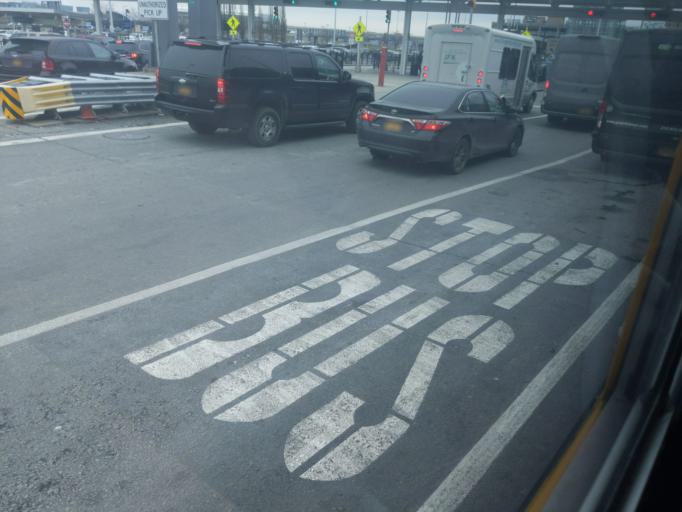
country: US
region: New York
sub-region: Nassau County
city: Inwood
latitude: 40.6431
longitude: -73.7833
